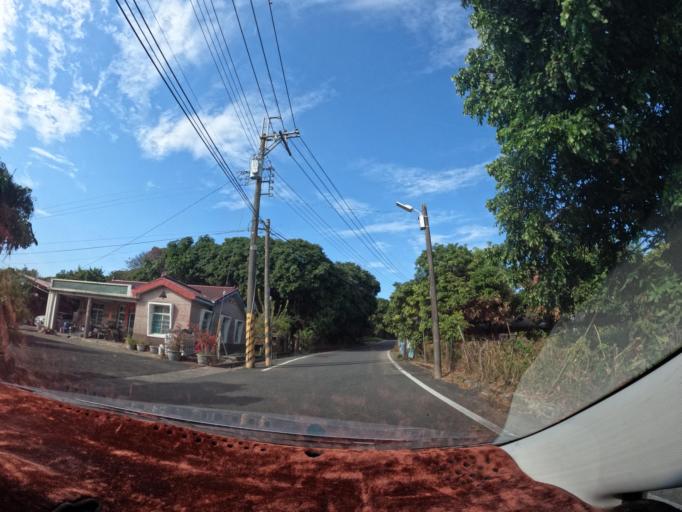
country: TW
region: Taiwan
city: Yujing
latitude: 23.0472
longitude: 120.4010
